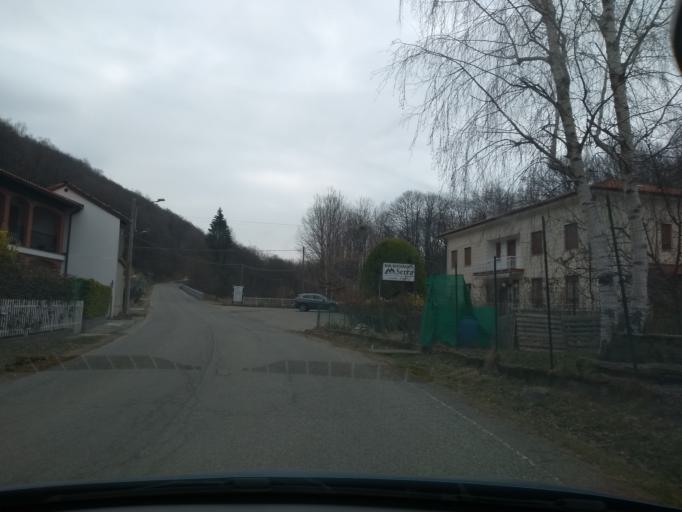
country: IT
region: Piedmont
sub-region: Provincia di Torino
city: Palazzo Canavese
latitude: 45.4748
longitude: 7.9692
